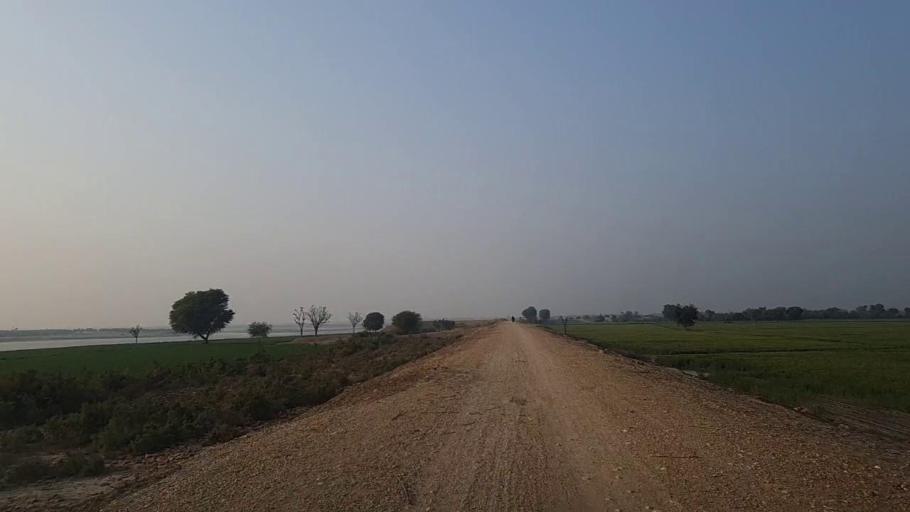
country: PK
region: Sindh
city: Sann
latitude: 26.1294
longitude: 68.1399
